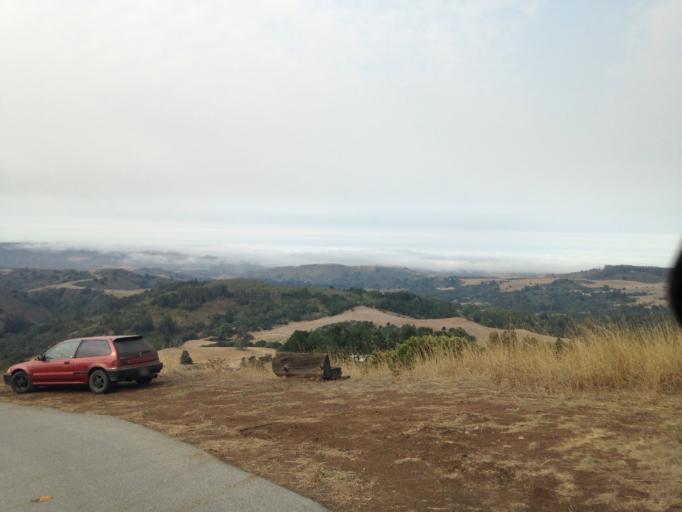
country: US
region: California
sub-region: San Mateo County
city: Portola Valley
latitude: 37.3675
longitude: -122.3031
